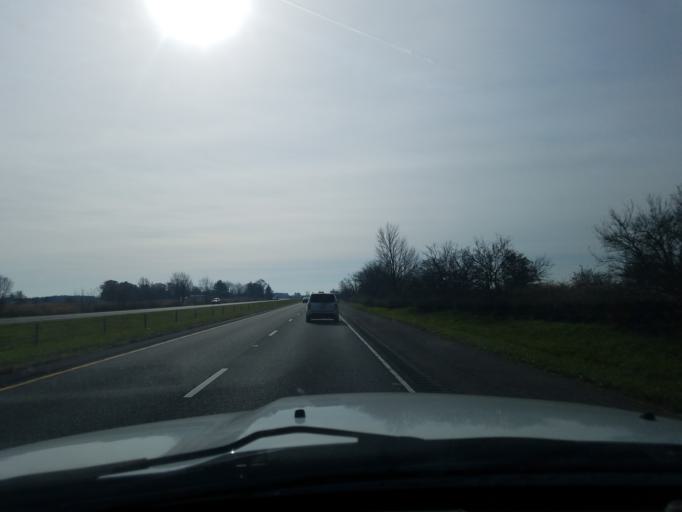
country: US
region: Indiana
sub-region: Delaware County
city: Daleville
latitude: 40.1780
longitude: -85.5645
